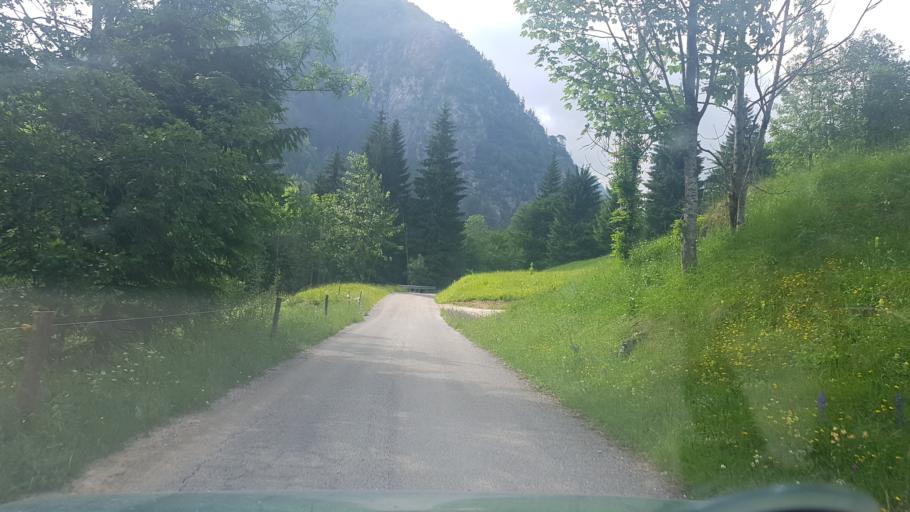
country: IT
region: Friuli Venezia Giulia
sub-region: Provincia di Udine
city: Paularo
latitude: 46.5282
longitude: 13.2124
